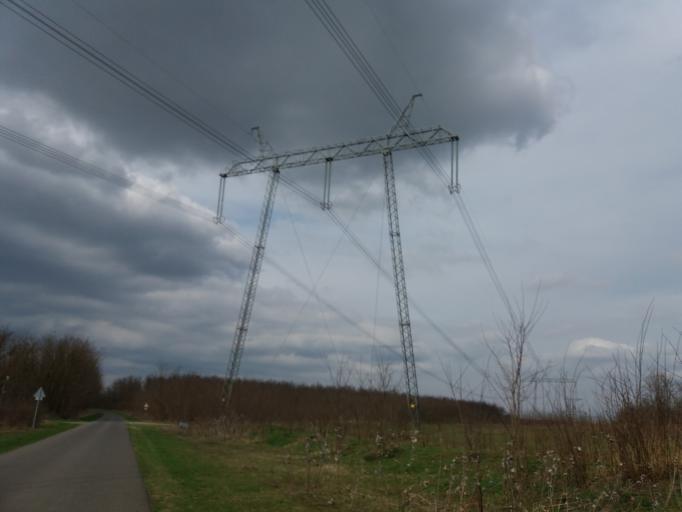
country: HU
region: Szabolcs-Szatmar-Bereg
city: Petnehaza
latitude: 48.0763
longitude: 22.0434
